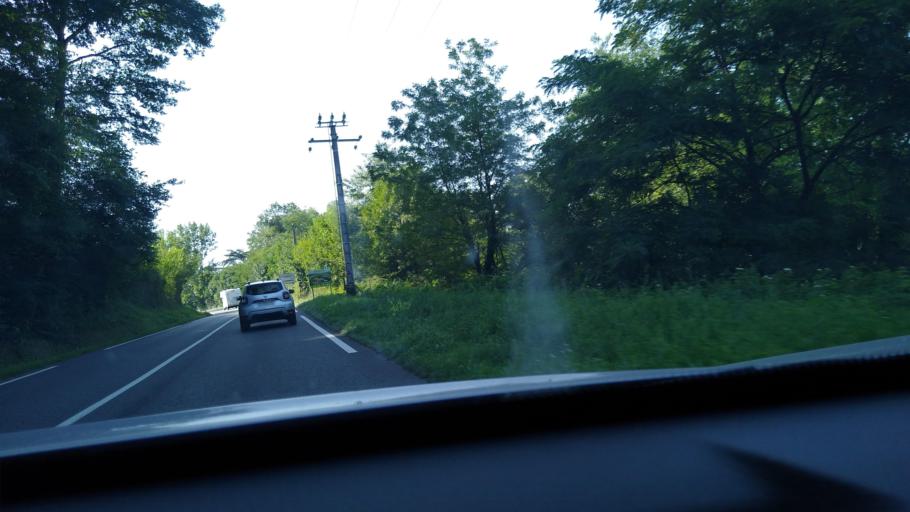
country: FR
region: Midi-Pyrenees
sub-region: Departement de la Haute-Garonne
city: Salies-du-Salat
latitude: 43.0781
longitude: 0.9577
